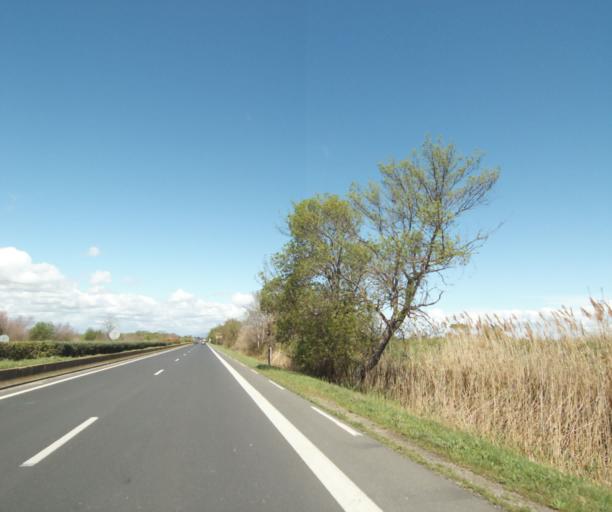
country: FR
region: Languedoc-Roussillon
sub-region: Departement de l'Herault
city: Lattes
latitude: 43.5438
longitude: 3.8964
